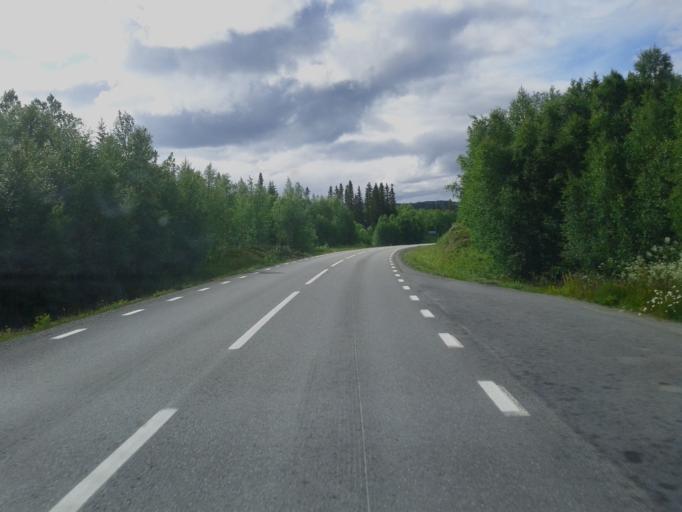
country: NO
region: Nordland
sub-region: Rana
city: Mo i Rana
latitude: 65.7123
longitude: 15.2209
